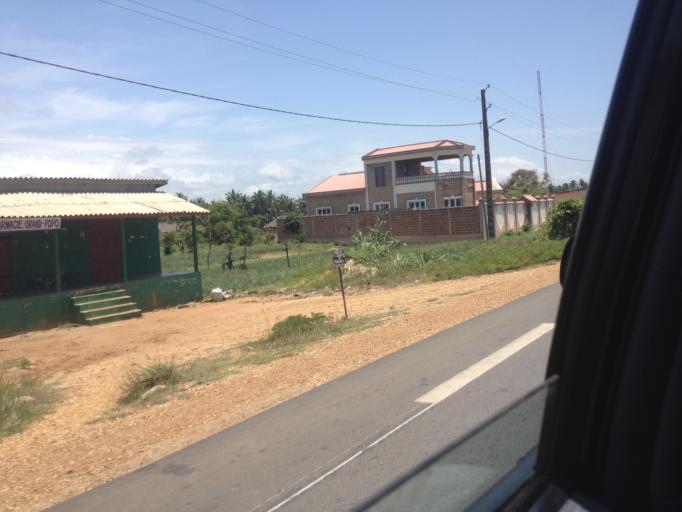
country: BJ
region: Mono
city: Grand-Popo
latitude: 6.2724
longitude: 1.7946
